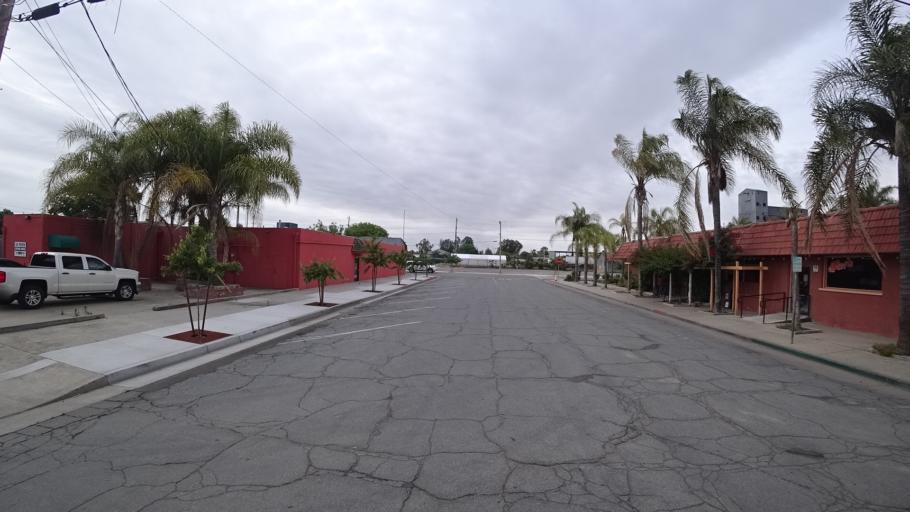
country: US
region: California
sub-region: Kings County
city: Hanford
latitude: 36.3268
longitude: -119.6407
